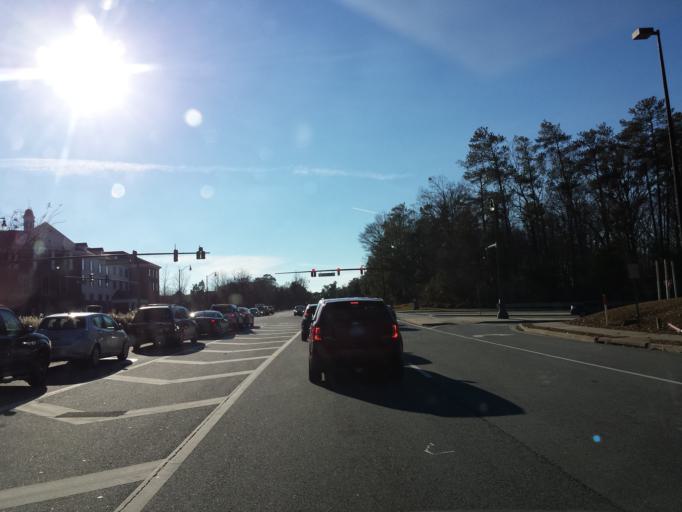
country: US
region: Georgia
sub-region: DeKalb County
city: Dunwoody
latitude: 33.9318
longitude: -84.3537
